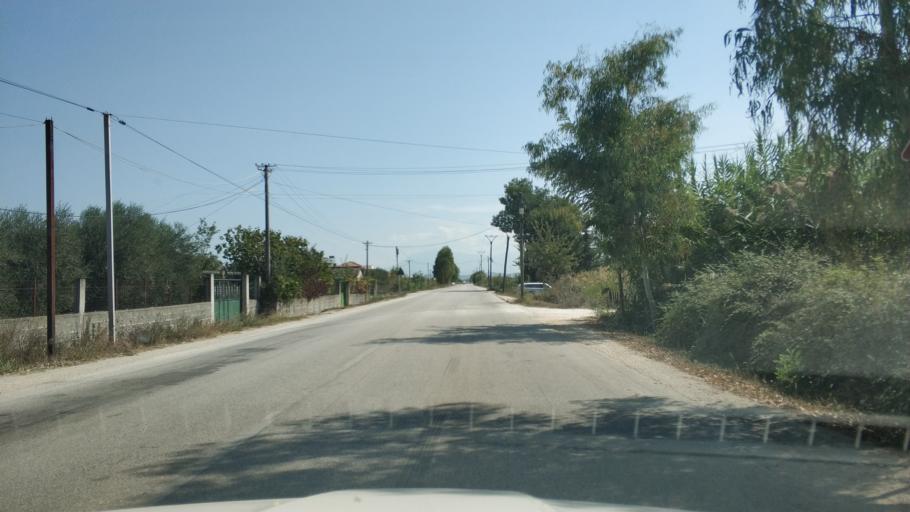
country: AL
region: Fier
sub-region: Rrethi i Lushnjes
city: Krutja e Poshtme
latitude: 40.8864
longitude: 19.6508
